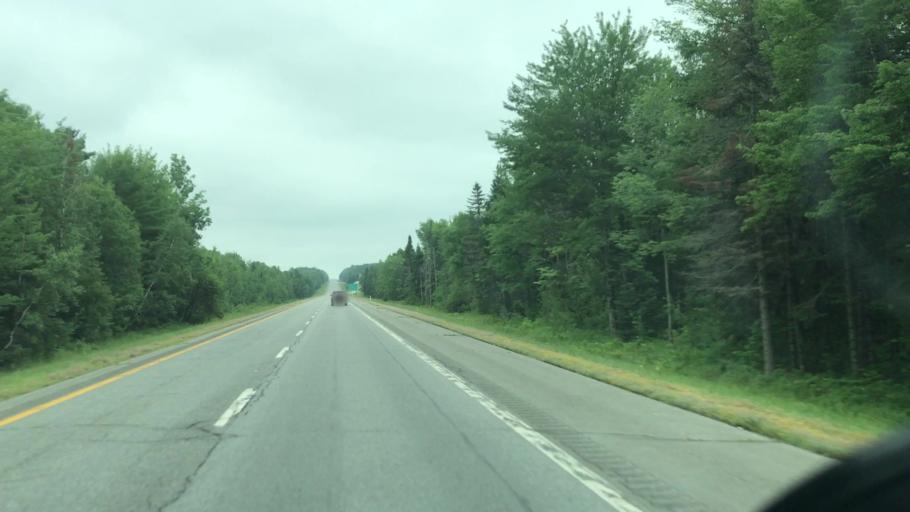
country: US
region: Maine
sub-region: Penobscot County
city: Milford
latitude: 44.9845
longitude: -68.7041
